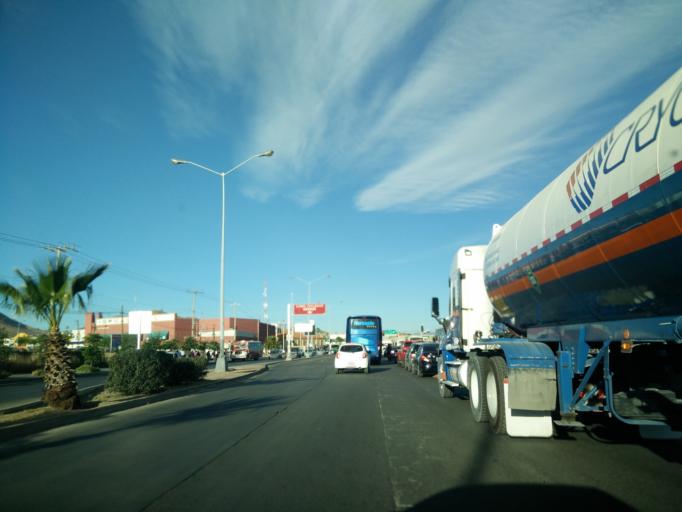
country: MX
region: Chihuahua
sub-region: Chihuahua
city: Chihuahua
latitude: 28.6237
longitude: -106.0273
